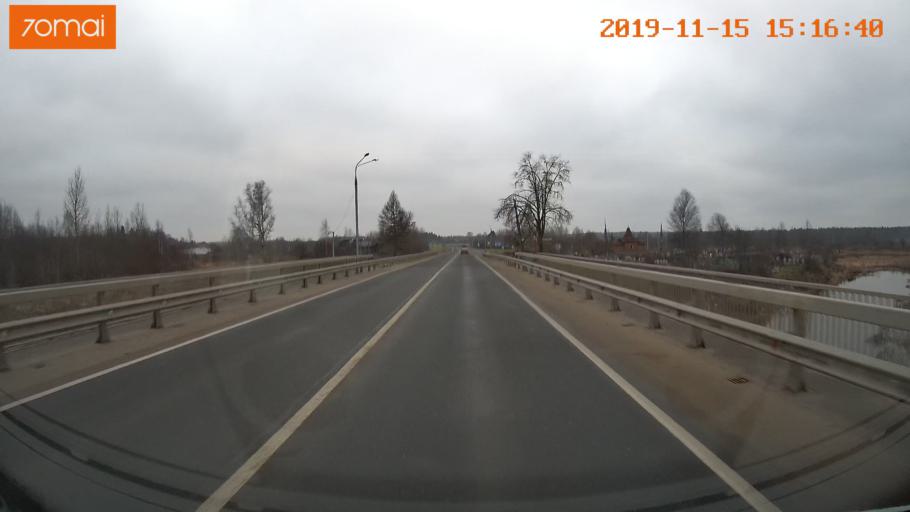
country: RU
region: Jaroslavl
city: Danilov
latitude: 58.2706
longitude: 40.1887
